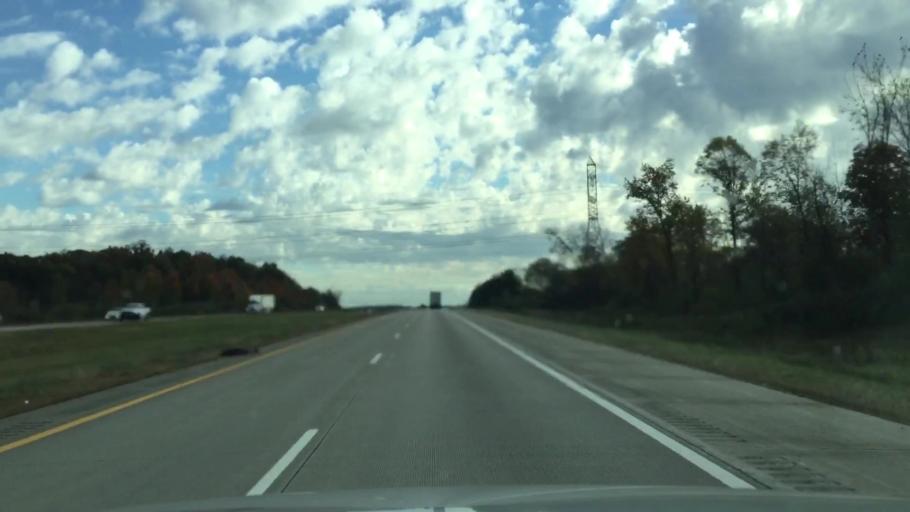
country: US
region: Michigan
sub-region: Genesee County
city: Davison
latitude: 43.0137
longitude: -83.4863
